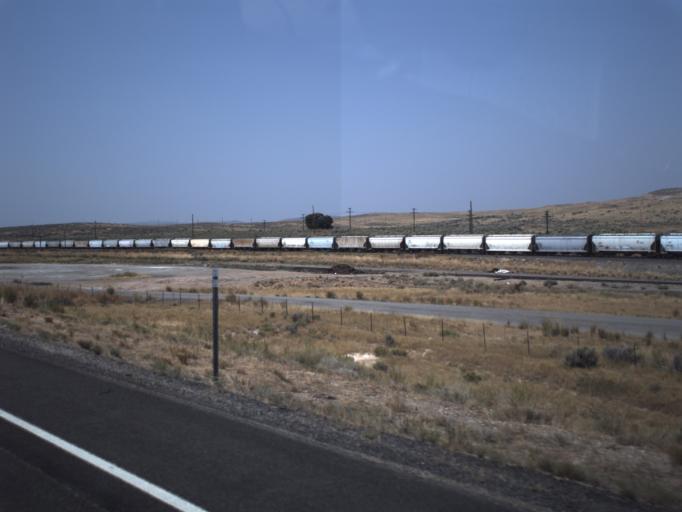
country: US
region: Wyoming
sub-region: Uinta County
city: Evanston
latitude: 41.2031
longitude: -111.1058
